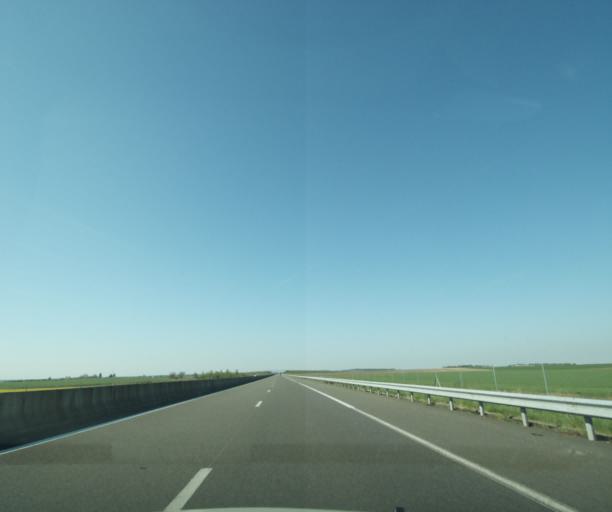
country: FR
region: Centre
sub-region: Departement du Loiret
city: Chilleurs-aux-Bois
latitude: 48.1068
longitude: 2.1274
